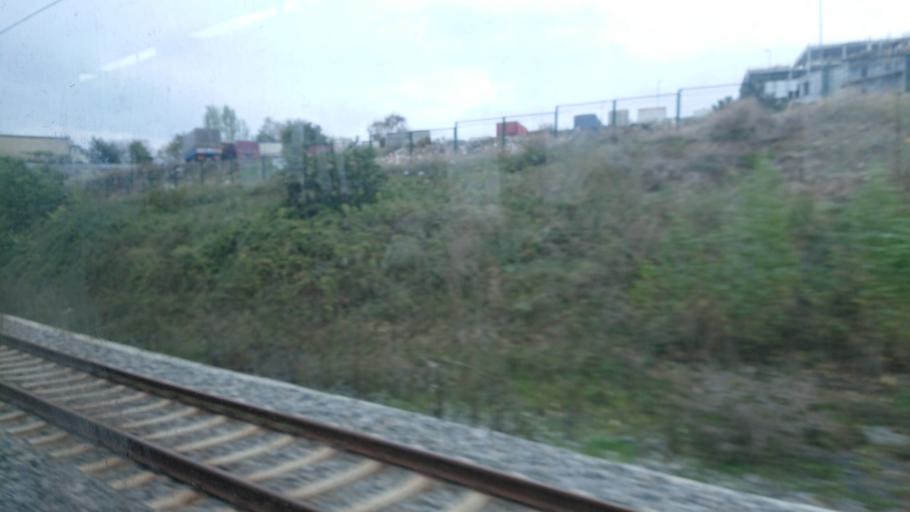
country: TR
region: Istanbul
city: Mahmutbey
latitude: 41.0121
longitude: 28.7688
